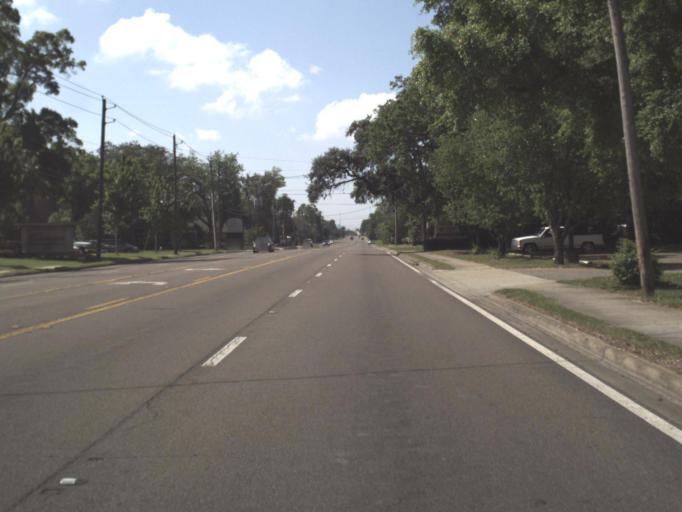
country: US
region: Florida
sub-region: Escambia County
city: Brent
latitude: 30.4664
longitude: -87.2245
